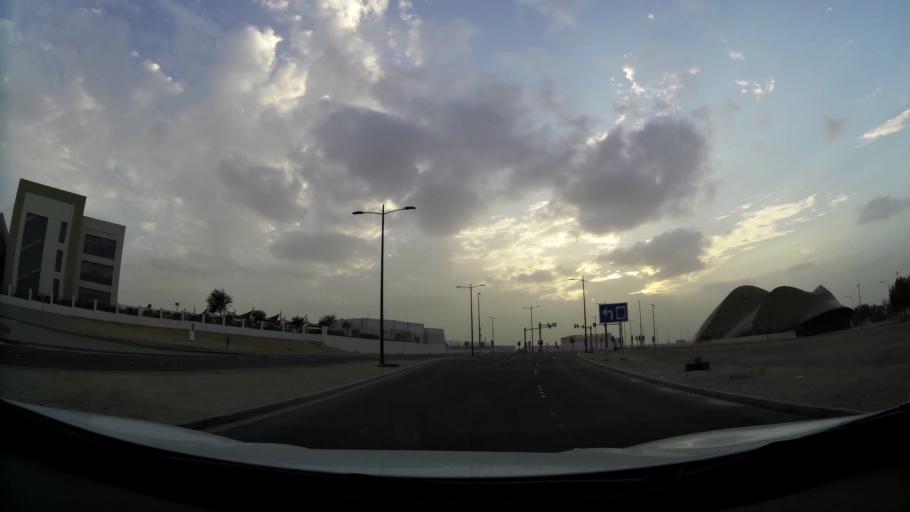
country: AE
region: Abu Dhabi
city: Abu Dhabi
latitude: 24.5331
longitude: 54.4199
